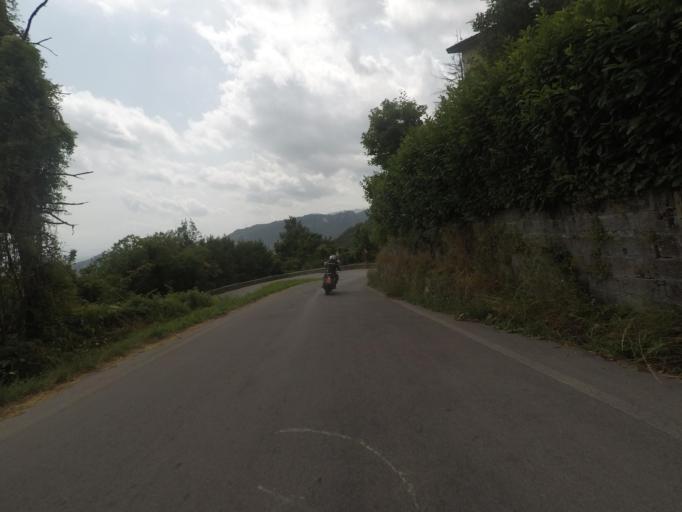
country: IT
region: Tuscany
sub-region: Provincia di Lucca
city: Castelnuovo di Garfagnana
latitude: 44.1063
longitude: 10.3743
